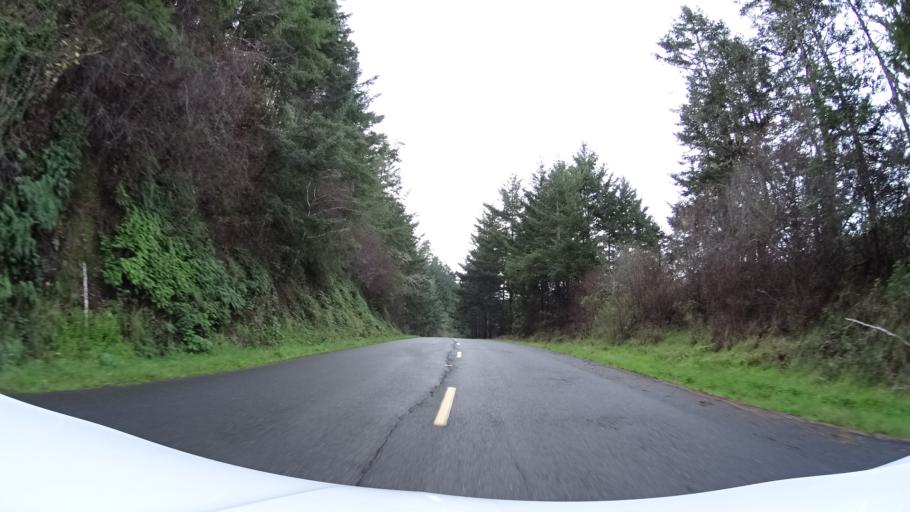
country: US
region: California
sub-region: Humboldt County
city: Ferndale
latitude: 40.3461
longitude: -124.3476
